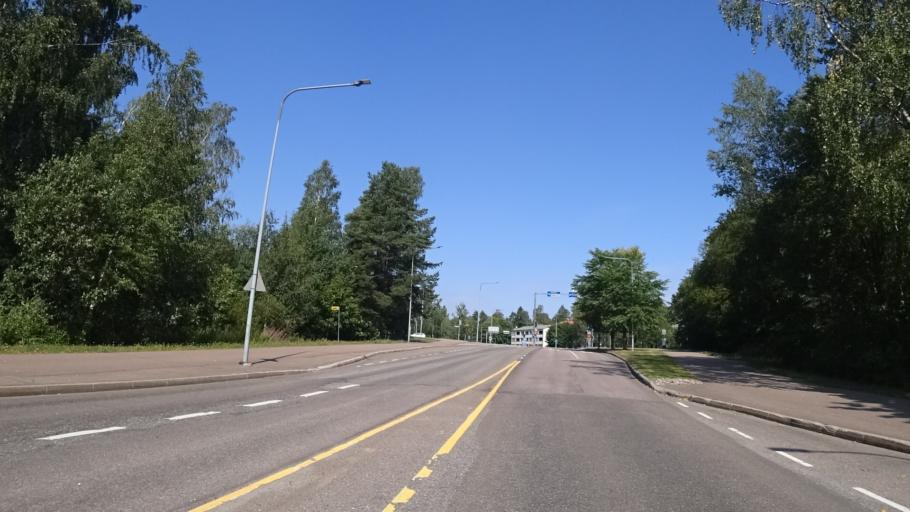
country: FI
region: Kymenlaakso
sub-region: Kotka-Hamina
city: Karhula
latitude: 60.5143
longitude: 26.9462
